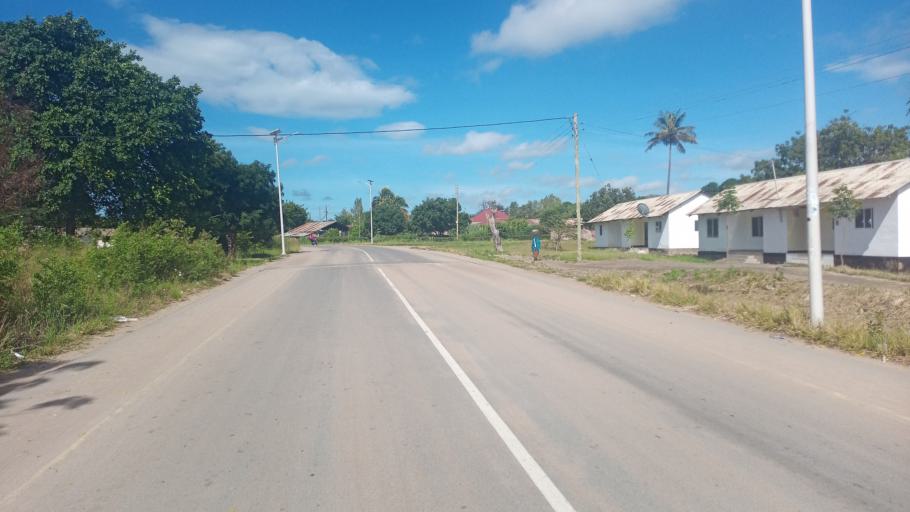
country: TZ
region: Dodoma
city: Dodoma
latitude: -6.1811
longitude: 35.7385
